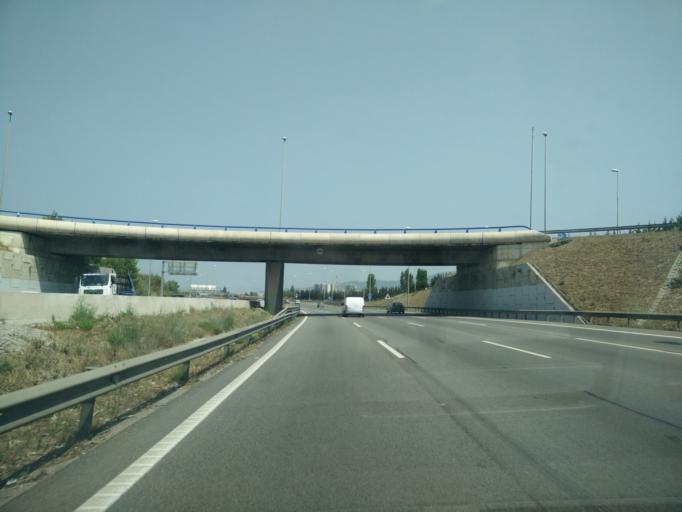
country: ES
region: Catalonia
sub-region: Provincia de Barcelona
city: Sant Joan Despi
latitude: 41.3629
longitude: 2.0505
